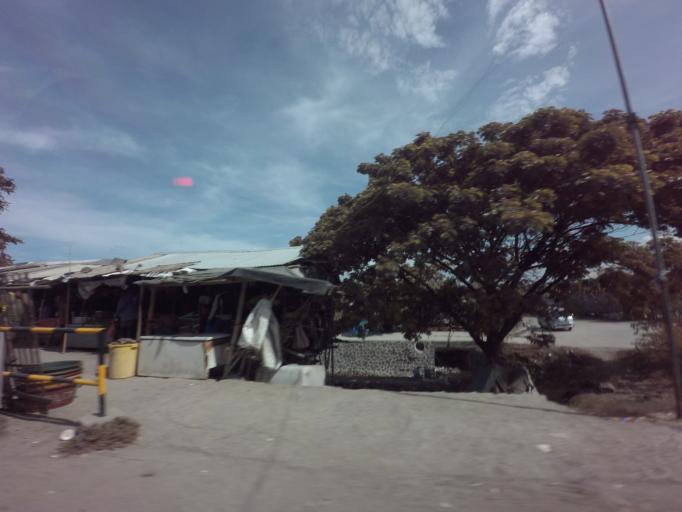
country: PH
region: Calabarzon
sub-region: Province of Rizal
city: Taguig
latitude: 14.5348
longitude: 121.1014
